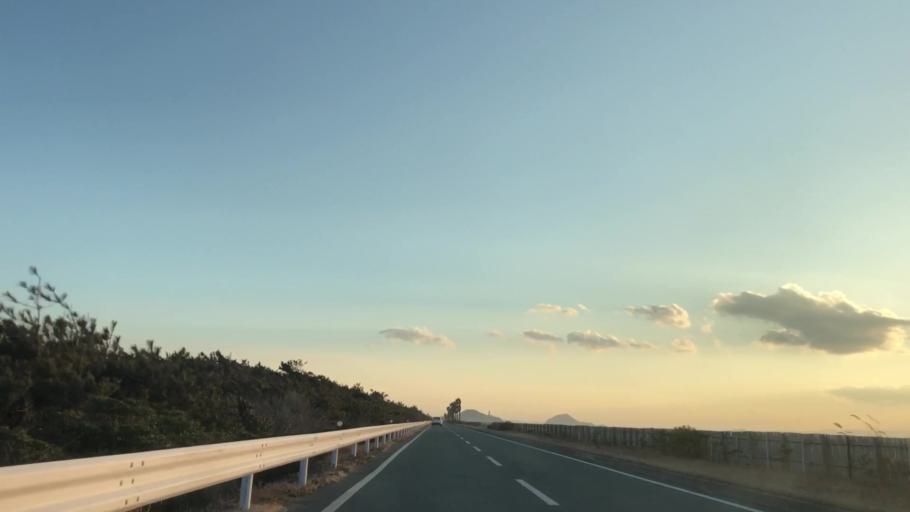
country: JP
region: Aichi
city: Toyohama
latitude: 34.6303
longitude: 137.0480
